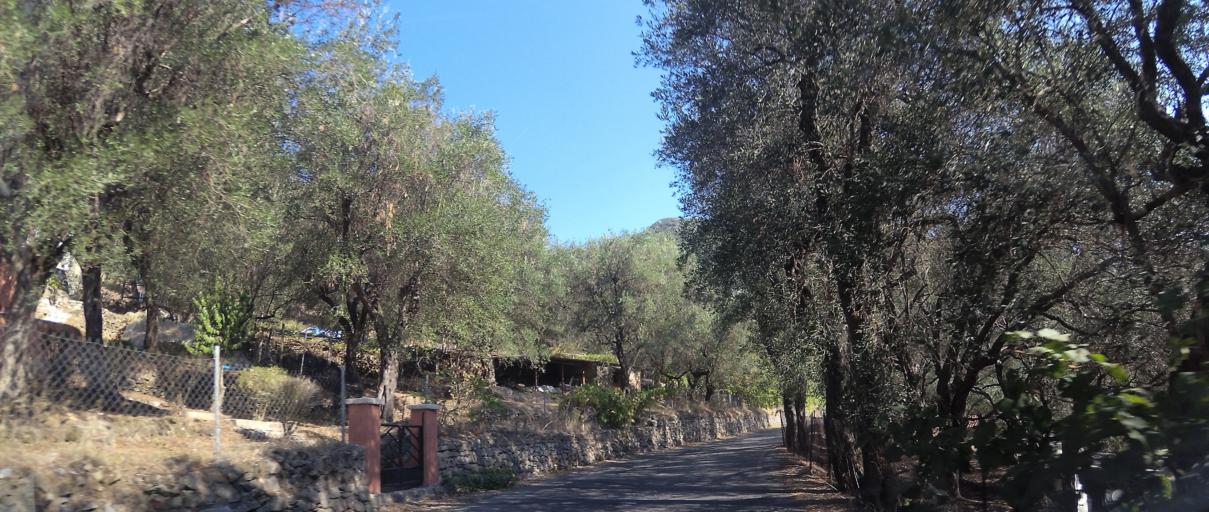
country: GR
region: Ionian Islands
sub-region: Nomos Kerkyras
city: Kontokali
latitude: 39.7204
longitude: 19.8466
